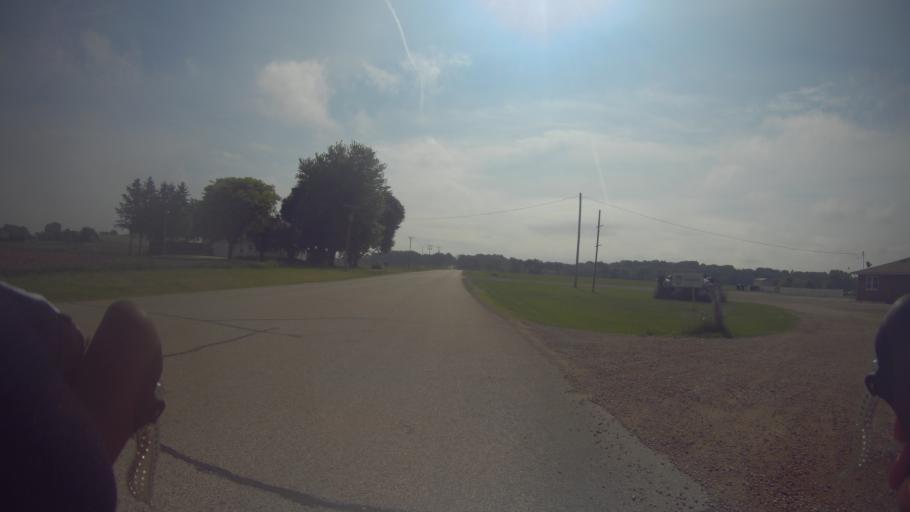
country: US
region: Wisconsin
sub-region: Dane County
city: Stoughton
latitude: 42.9917
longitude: -89.2003
